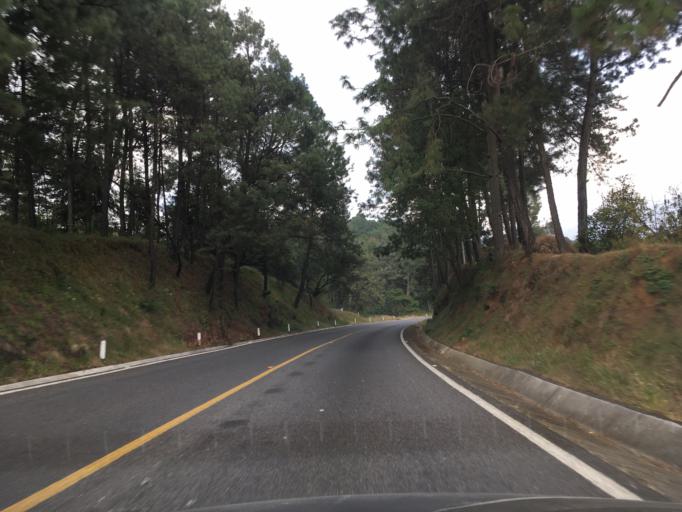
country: MX
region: Michoacan
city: Tingambato
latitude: 19.4828
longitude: -101.8951
